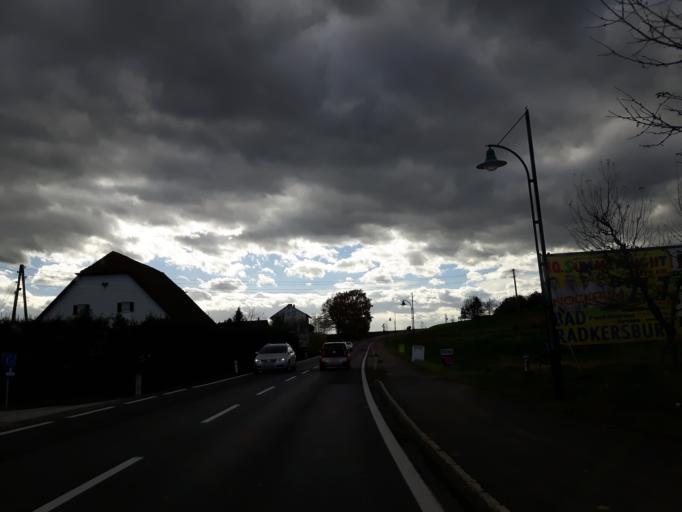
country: AT
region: Styria
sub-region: Politischer Bezirk Suedoststeiermark
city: Kirchbach in Steiermark
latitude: 46.9118
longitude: 15.6721
